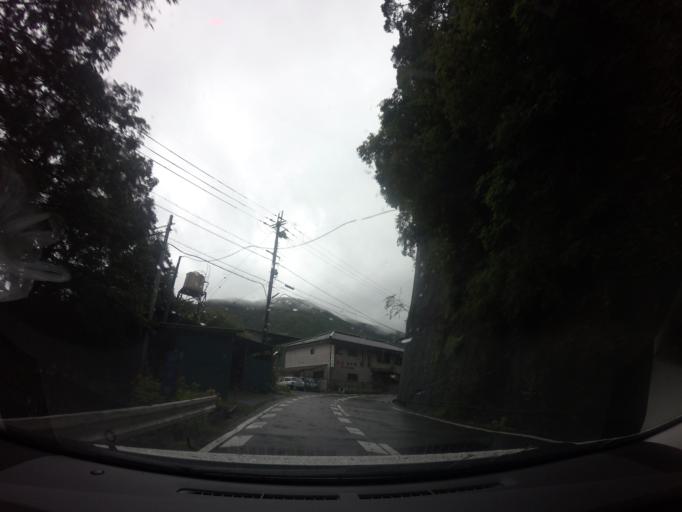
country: JP
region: Wakayama
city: Koya
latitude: 34.0606
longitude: 135.7488
